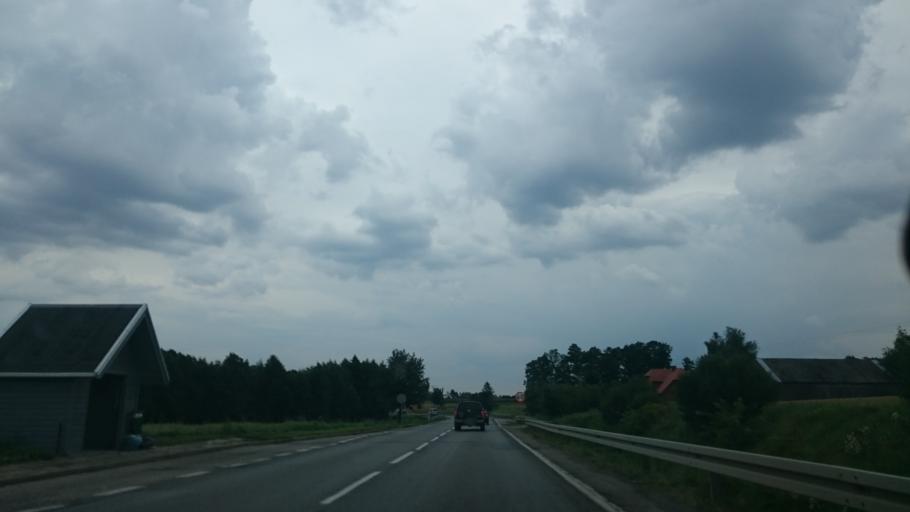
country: PL
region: Kujawsko-Pomorskie
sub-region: Powiat tucholski
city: Lubiewo
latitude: 53.5093
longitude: 17.9757
